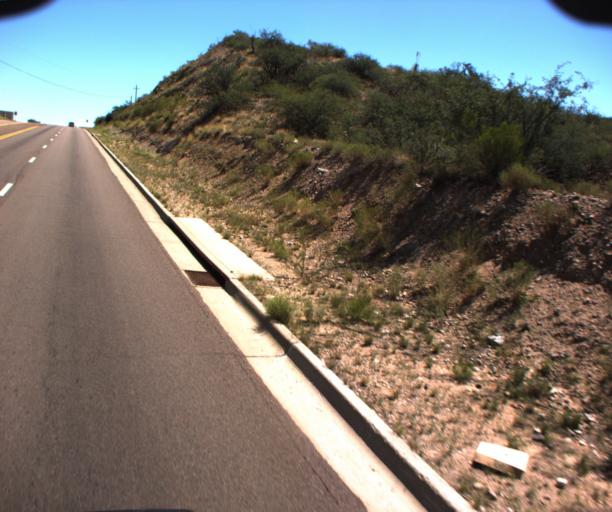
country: US
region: Arizona
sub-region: Gila County
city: Globe
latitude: 33.3936
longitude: -110.7611
